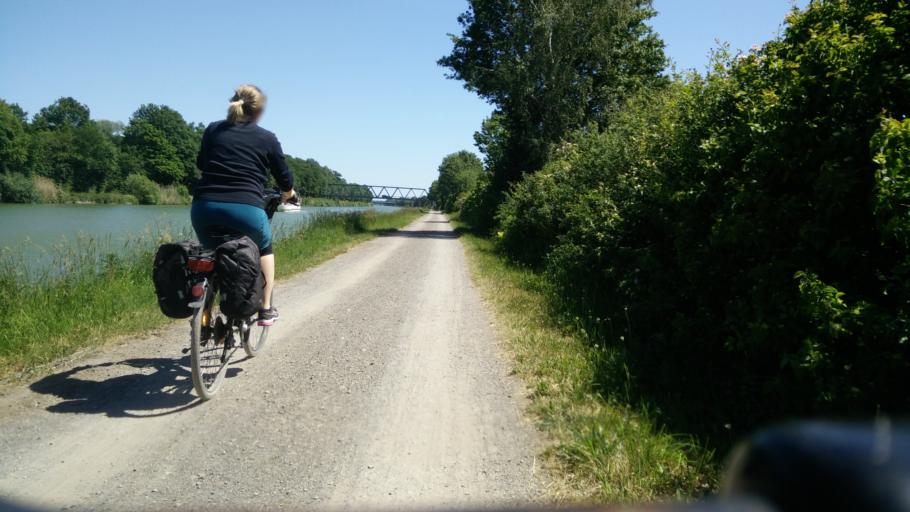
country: DE
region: Lower Saxony
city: Wunstorf
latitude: 52.3953
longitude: 9.4414
